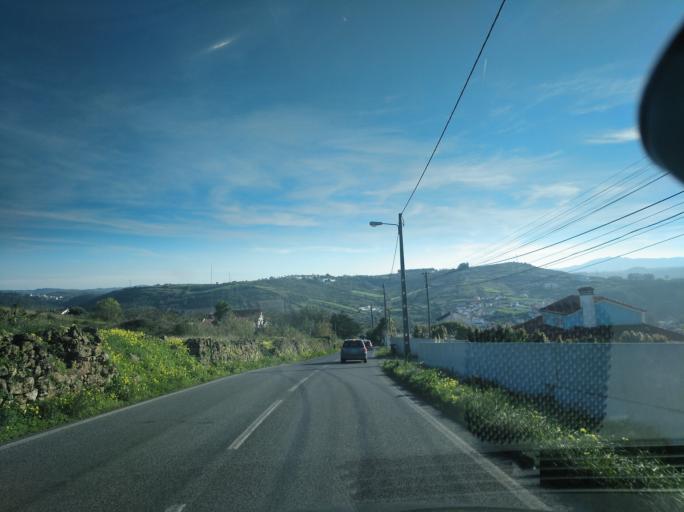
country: PT
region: Lisbon
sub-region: Sintra
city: Pero Pinheiro
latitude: 38.8947
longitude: -9.3269
